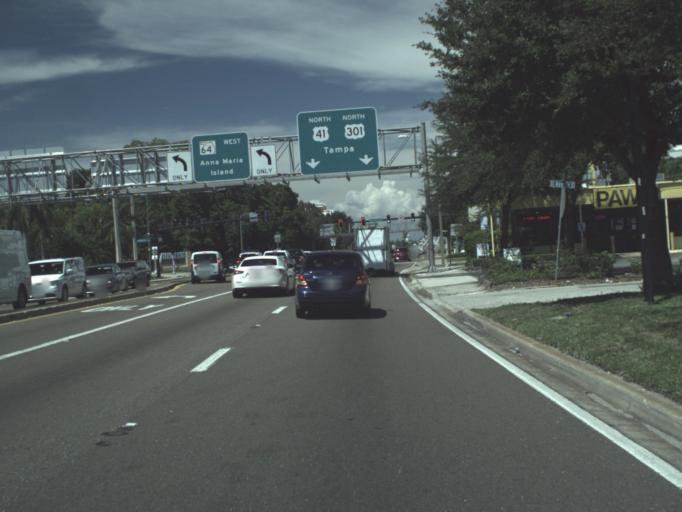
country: US
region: Florida
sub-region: Manatee County
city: Bradenton
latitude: 27.4941
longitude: -82.5629
